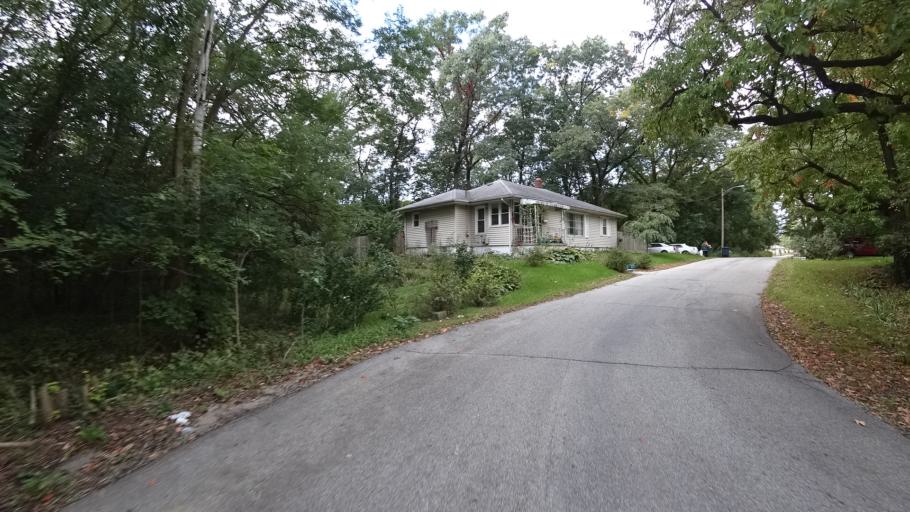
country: US
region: Indiana
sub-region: LaPorte County
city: Trail Creek
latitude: 41.7075
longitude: -86.8720
